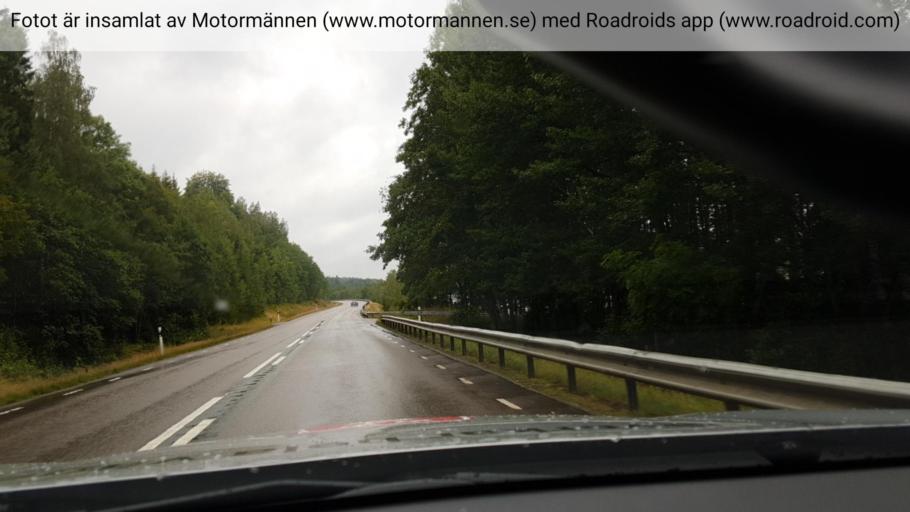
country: SE
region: Vaestra Goetaland
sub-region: Bengtsfors Kommun
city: Billingsfors
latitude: 58.9405
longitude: 12.1046
